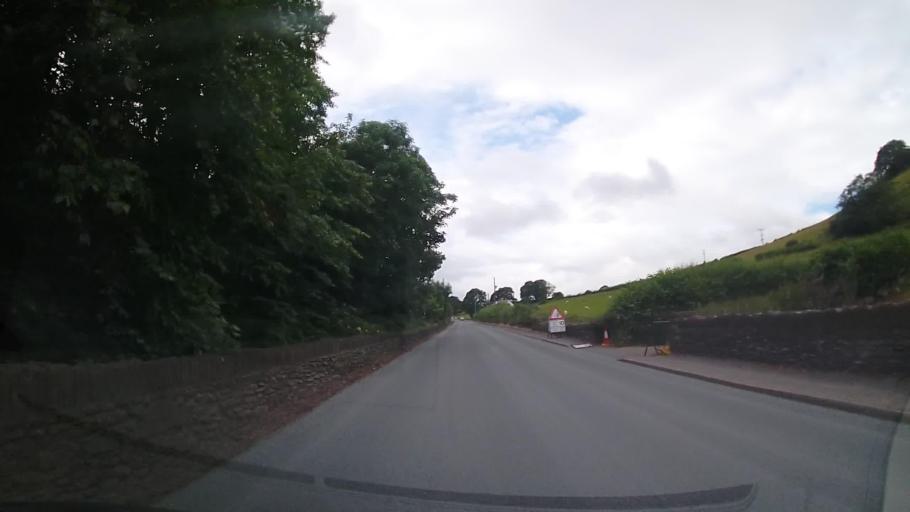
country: GB
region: Wales
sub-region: Denbighshire
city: Bryneglwys
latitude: 52.9712
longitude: -3.2452
